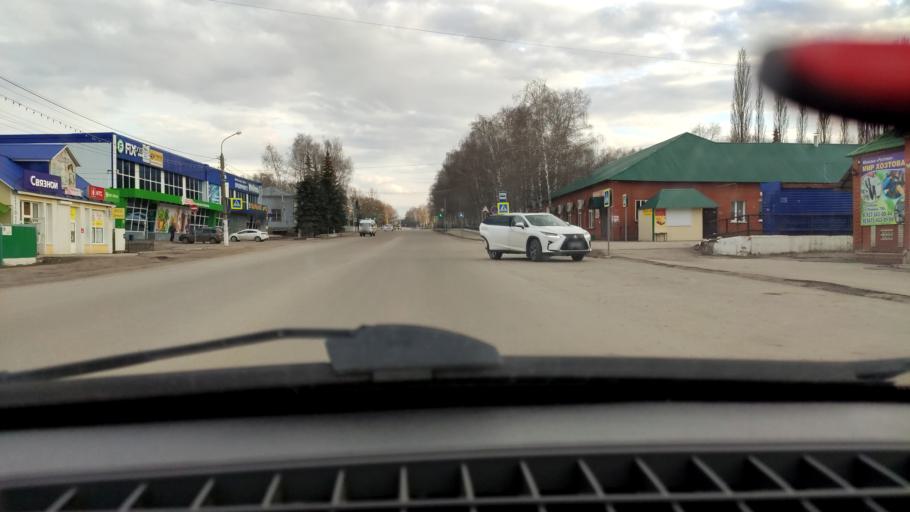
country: RU
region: Bashkortostan
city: Tolbazy
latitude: 54.0176
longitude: 55.8864
